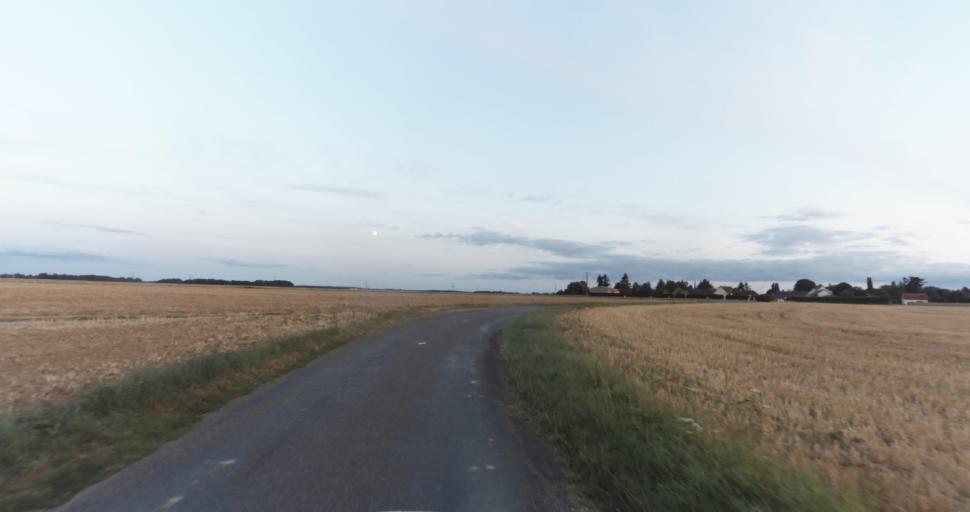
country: FR
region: Haute-Normandie
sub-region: Departement de l'Eure
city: Saint-Germain-sur-Avre
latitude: 48.8719
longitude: 1.2483
